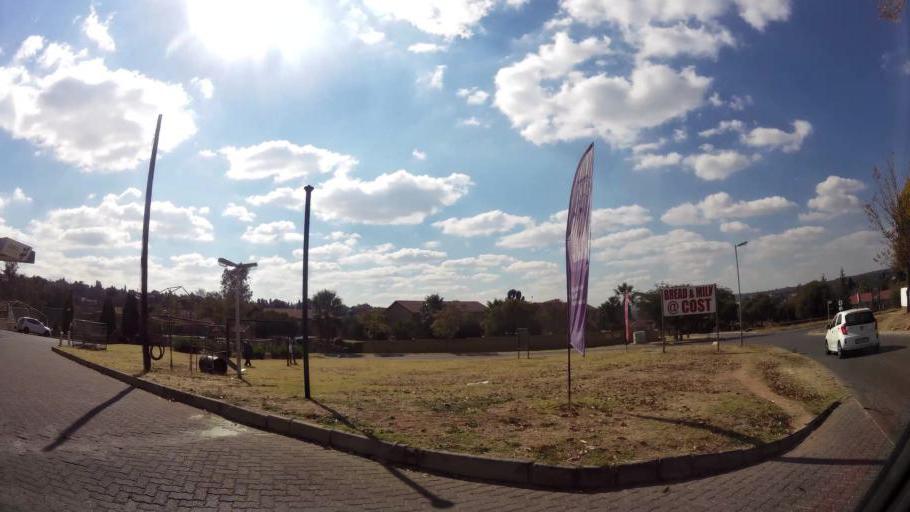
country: ZA
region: Gauteng
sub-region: City of Johannesburg Metropolitan Municipality
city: Roodepoort
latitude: -26.0712
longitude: 27.9634
